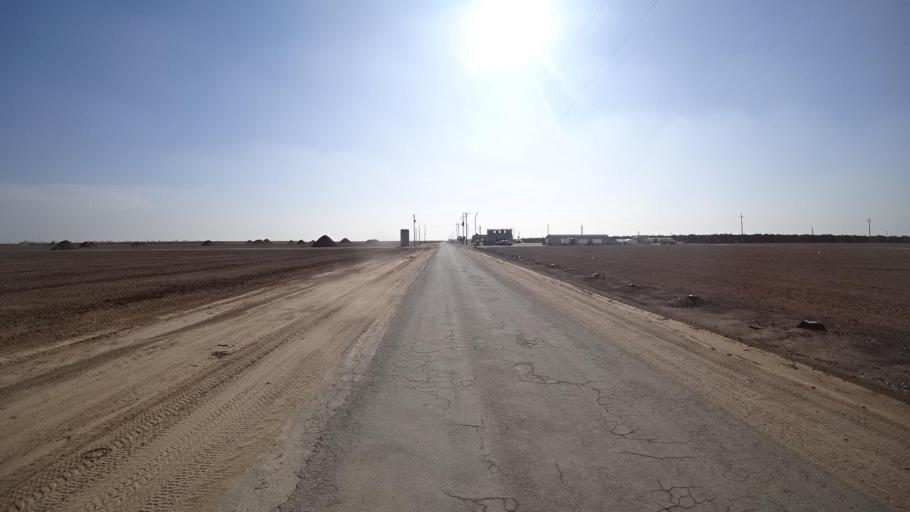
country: US
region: California
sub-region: Kern County
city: Shafter
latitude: 35.5380
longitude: -119.1336
